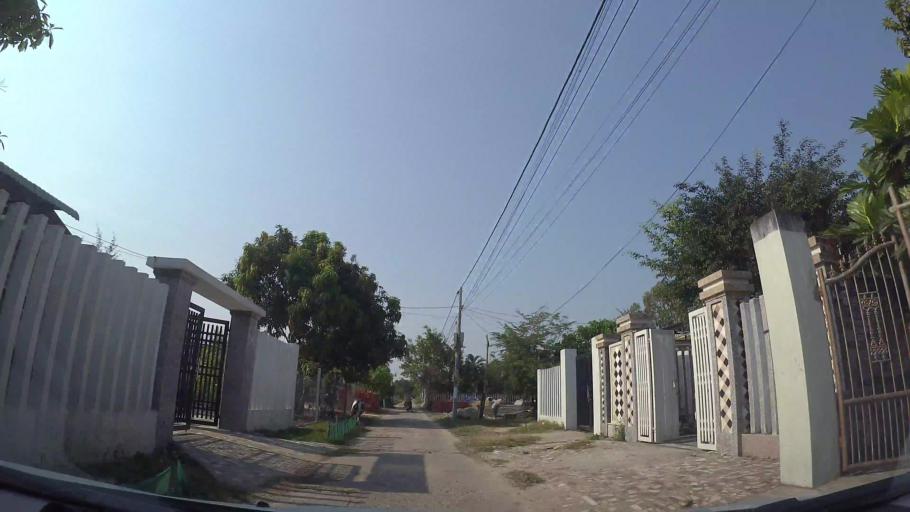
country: VN
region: Da Nang
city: Ngu Hanh Son
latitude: 15.9526
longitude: 108.2663
